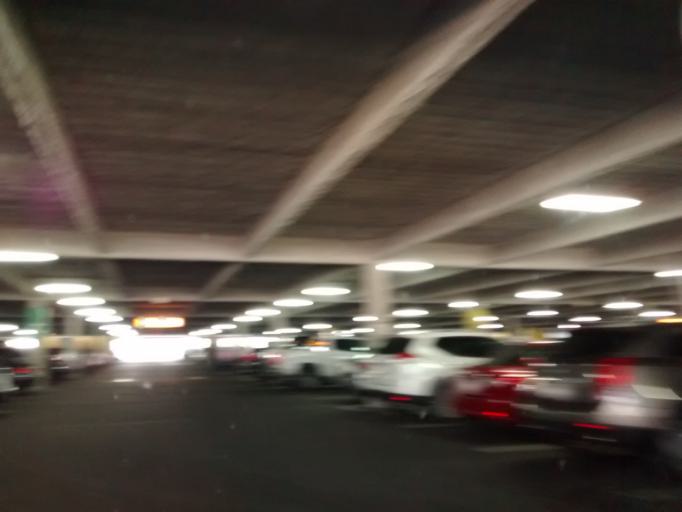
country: US
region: Massachusetts
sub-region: Norfolk County
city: Avon
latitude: 42.1388
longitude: -71.0680
